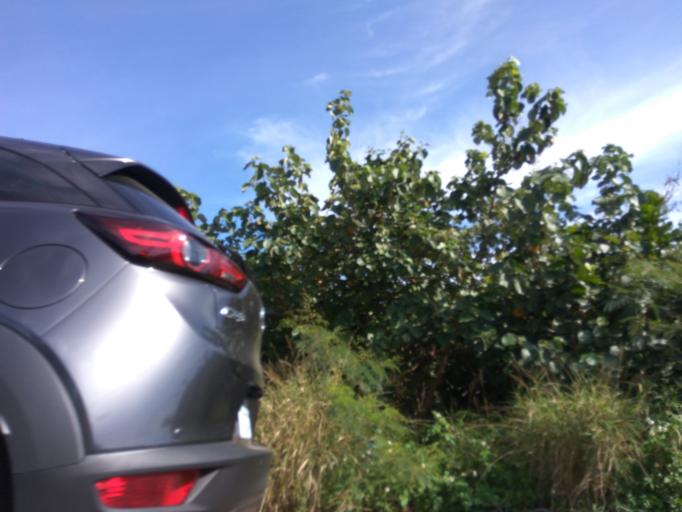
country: TW
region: Taiwan
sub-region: Hsinchu
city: Zhubei
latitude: 25.0403
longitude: 121.0642
